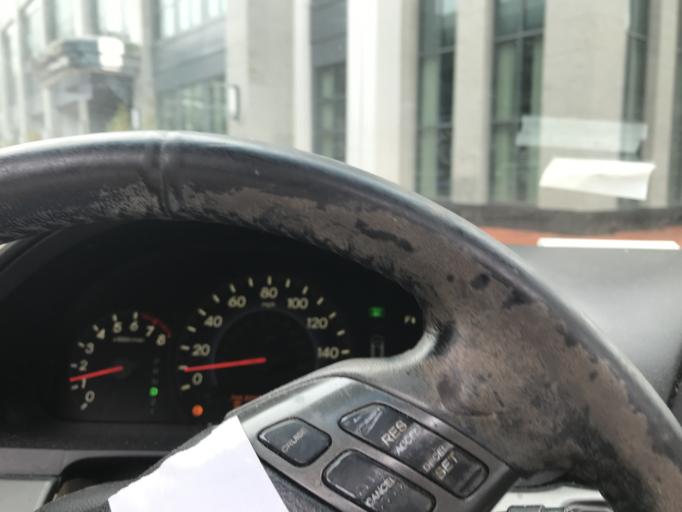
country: US
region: Louisiana
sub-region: Orleans Parish
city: New Orleans
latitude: 29.9428
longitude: -90.0700
